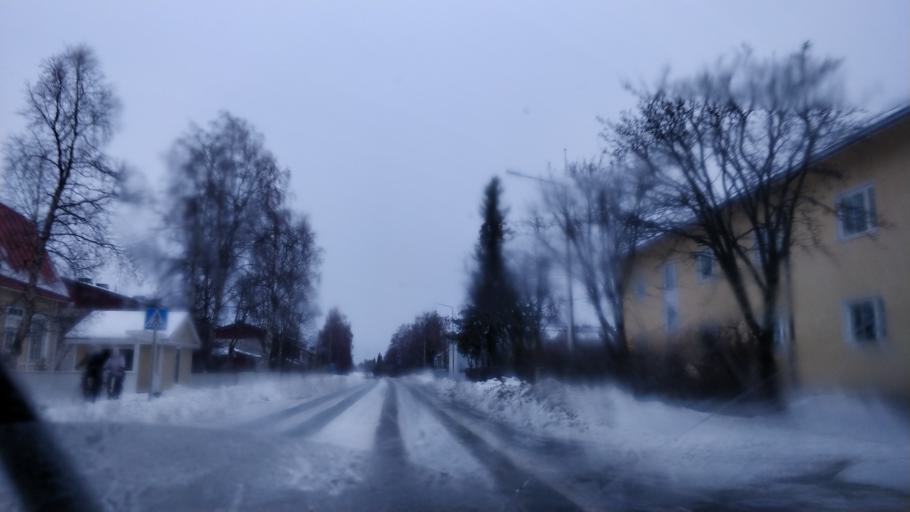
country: FI
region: Lapland
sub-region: Kemi-Tornio
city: Kemi
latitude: 65.7406
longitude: 24.5605
